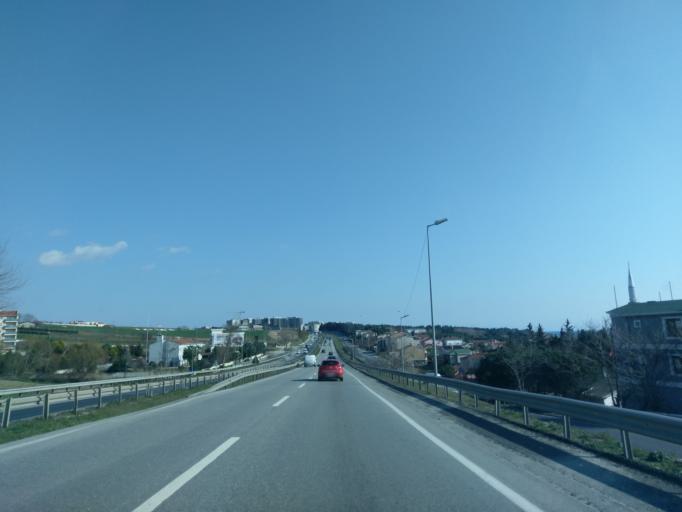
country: TR
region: Istanbul
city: Kumburgaz
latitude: 41.0112
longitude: 28.4988
